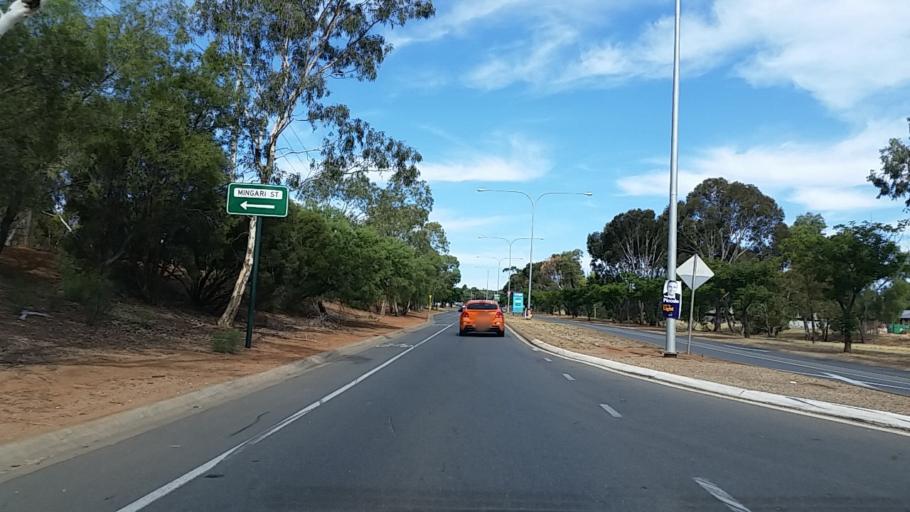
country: AU
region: South Australia
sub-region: Playford
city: Smithfield
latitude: -34.6771
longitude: 138.6926
